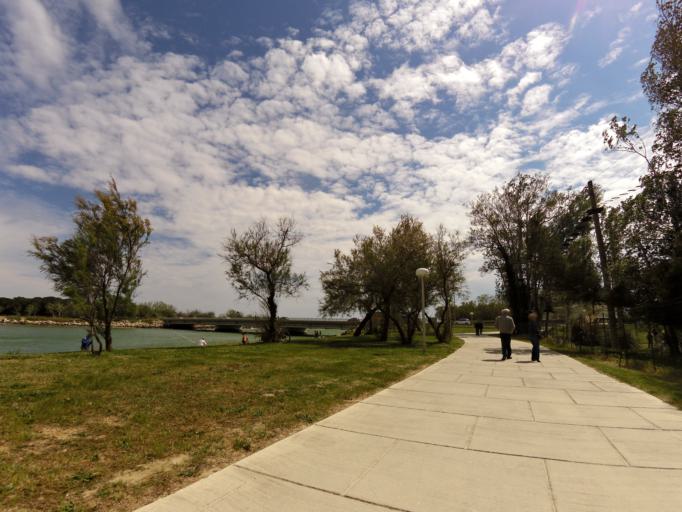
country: FR
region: Languedoc-Roussillon
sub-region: Departement de l'Herault
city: La Grande-Motte
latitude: 43.5573
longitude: 4.1008
